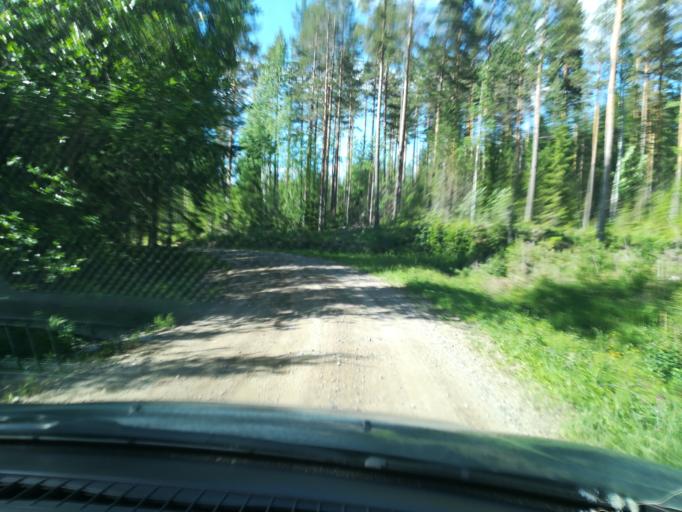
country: FI
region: Southern Savonia
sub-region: Mikkeli
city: Puumala
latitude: 61.6569
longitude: 28.1630
